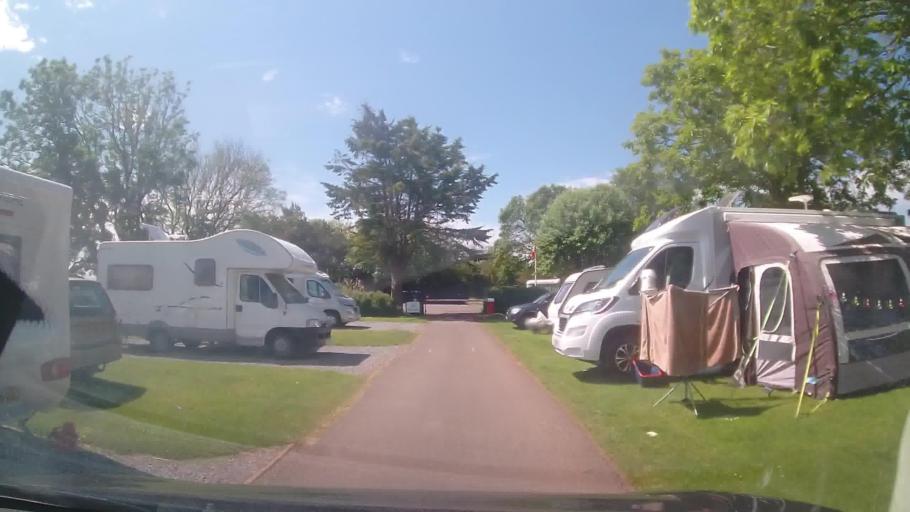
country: GB
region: England
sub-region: Devon
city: Dartmouth
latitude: 50.2912
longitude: -3.6504
